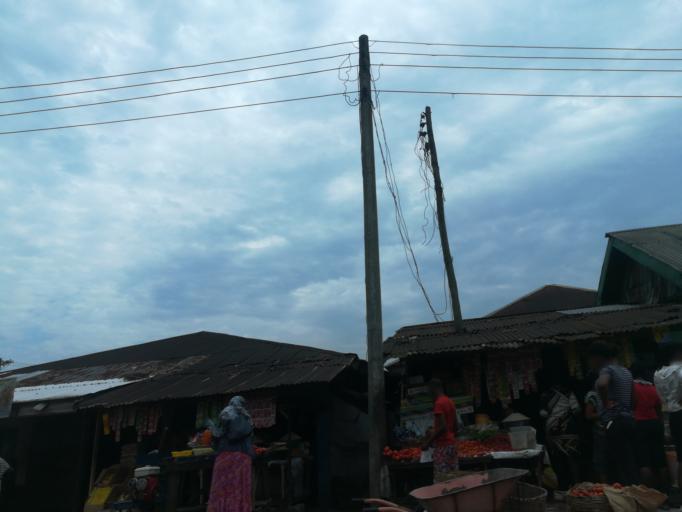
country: NG
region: Rivers
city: Port Harcourt
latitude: 4.8156
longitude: 6.9544
